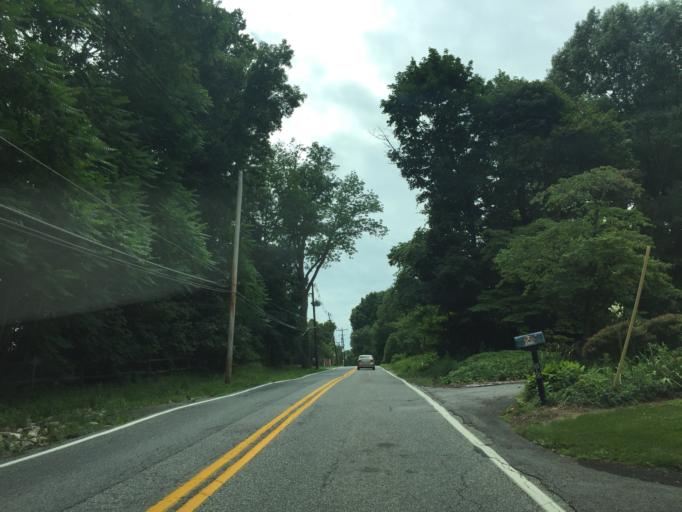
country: US
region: Maryland
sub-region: Baltimore County
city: Hampton
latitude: 39.4156
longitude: -76.5962
